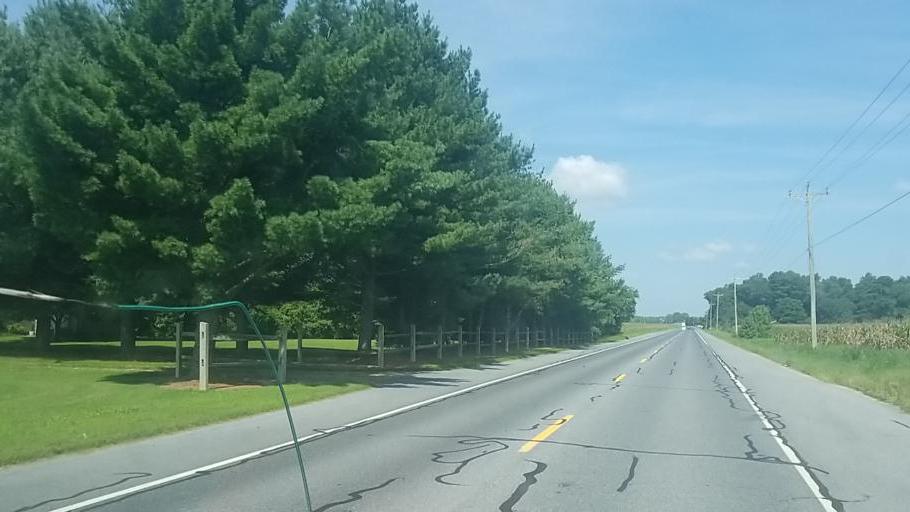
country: US
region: Delaware
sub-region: Sussex County
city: Seaford
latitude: 38.6788
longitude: -75.5814
